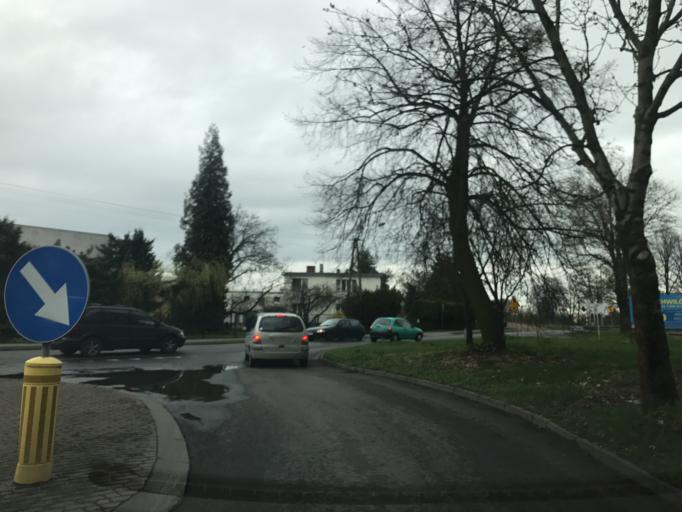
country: PL
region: Kujawsko-Pomorskie
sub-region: Powiat chelminski
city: Unislaw
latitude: 53.2080
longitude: 18.3880
